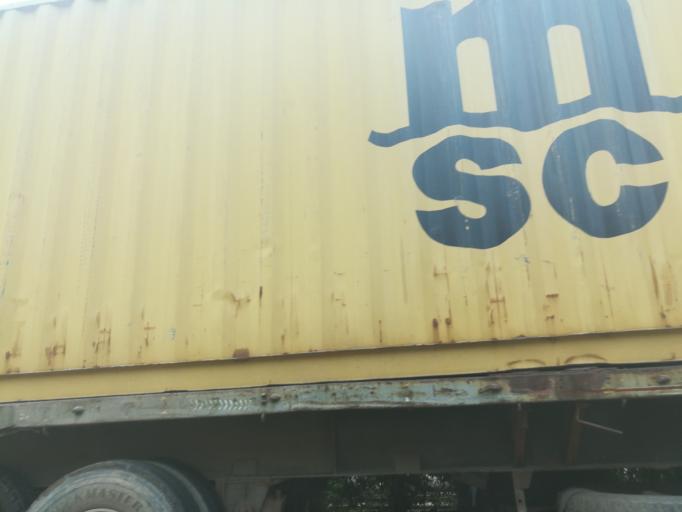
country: NG
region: Lagos
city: Ikeja
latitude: 6.6124
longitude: 3.3417
